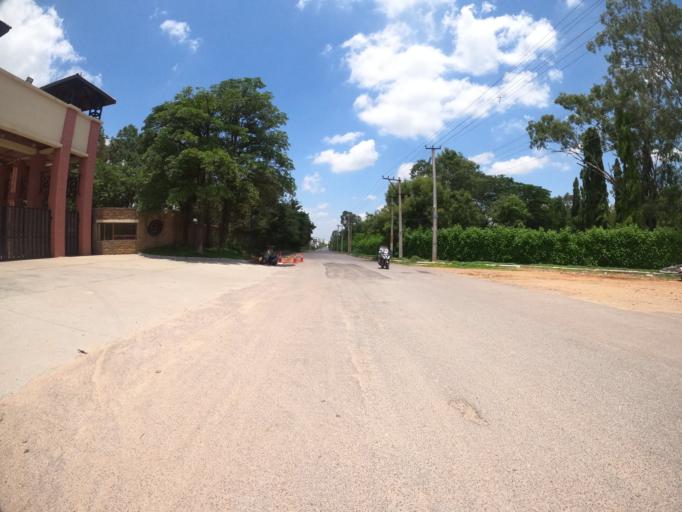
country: IN
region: Telangana
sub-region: Medak
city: Serilingampalle
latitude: 17.3895
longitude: 78.3150
